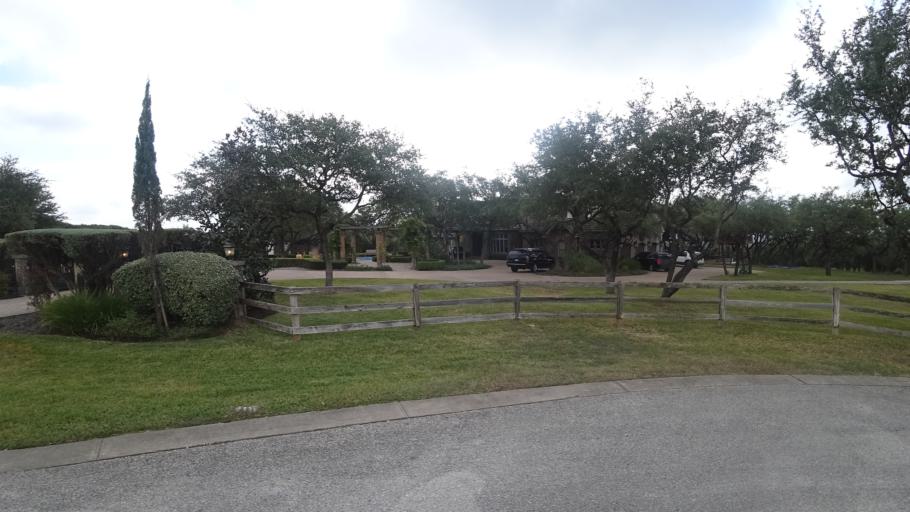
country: US
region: Texas
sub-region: Travis County
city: Barton Creek
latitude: 30.3037
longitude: -97.8973
